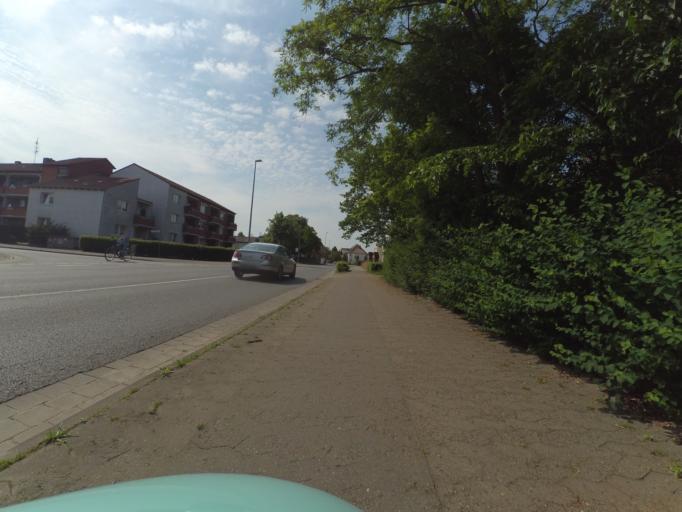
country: DE
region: Lower Saxony
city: Sehnde
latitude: 52.3154
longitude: 9.9639
